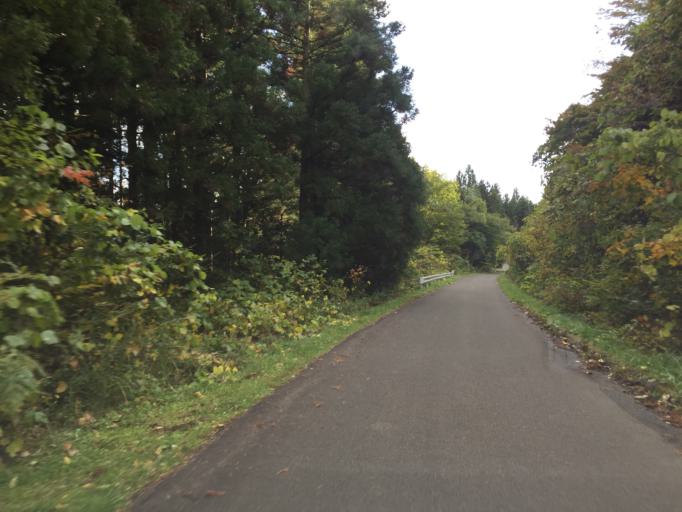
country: JP
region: Fukushima
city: Fukushima-shi
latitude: 37.7123
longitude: 140.3334
